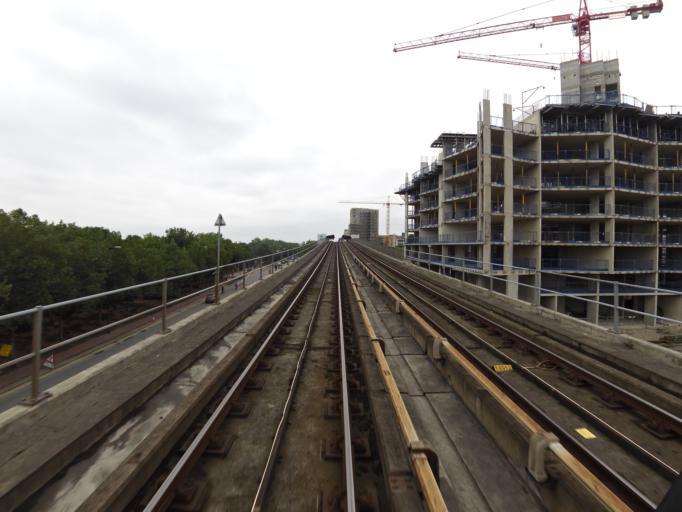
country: GB
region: England
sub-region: Greater London
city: Woolwich
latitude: 51.5021
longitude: 0.0295
